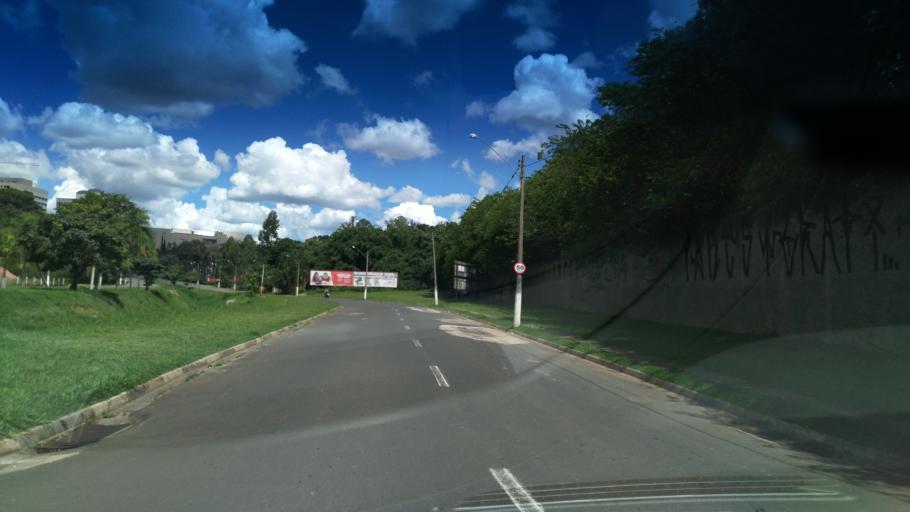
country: BR
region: Sao Paulo
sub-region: Valinhos
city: Valinhos
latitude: -22.9764
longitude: -47.0156
